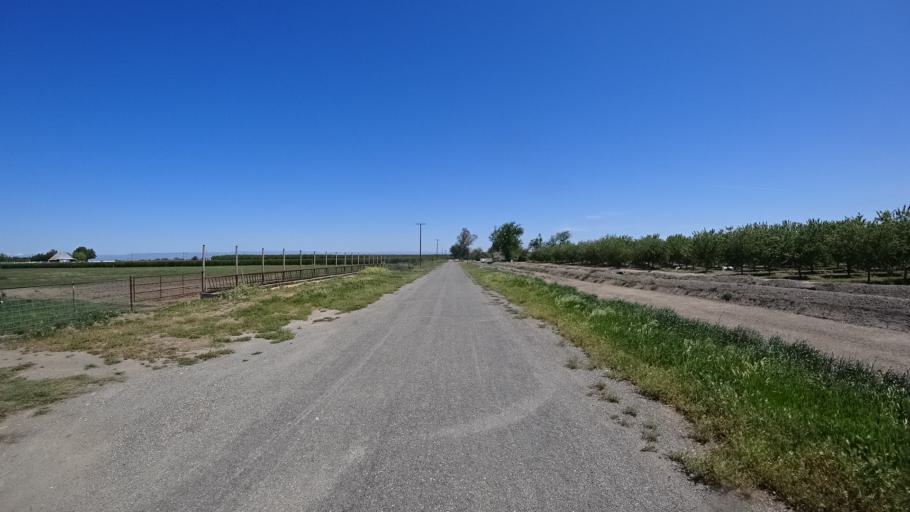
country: US
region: California
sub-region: Glenn County
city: Hamilton City
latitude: 39.7286
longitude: -122.0943
